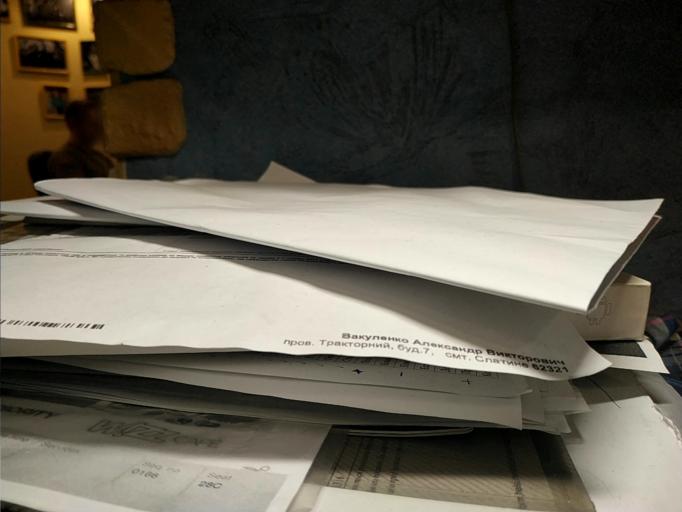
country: RU
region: Tverskaya
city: Zubtsov
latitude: 56.1094
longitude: 34.6354
